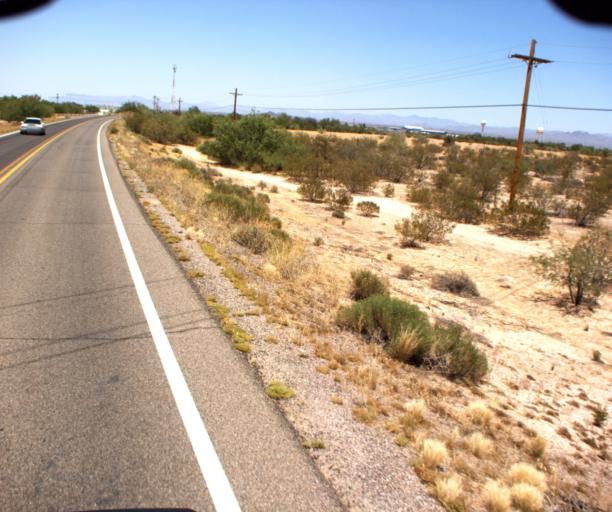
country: US
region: Arizona
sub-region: Pinal County
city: Florence
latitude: 33.0155
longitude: -111.3789
